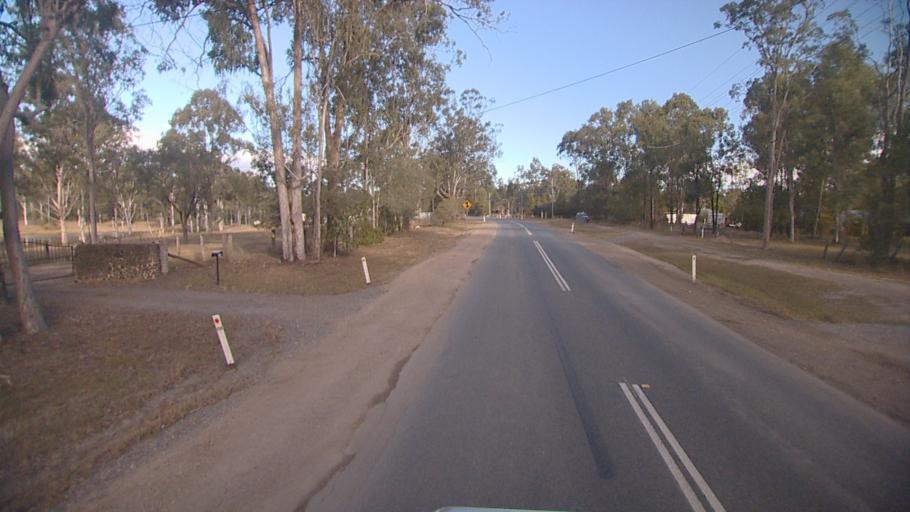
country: AU
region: Queensland
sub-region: Logan
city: Cedar Vale
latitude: -27.8523
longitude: 153.0521
